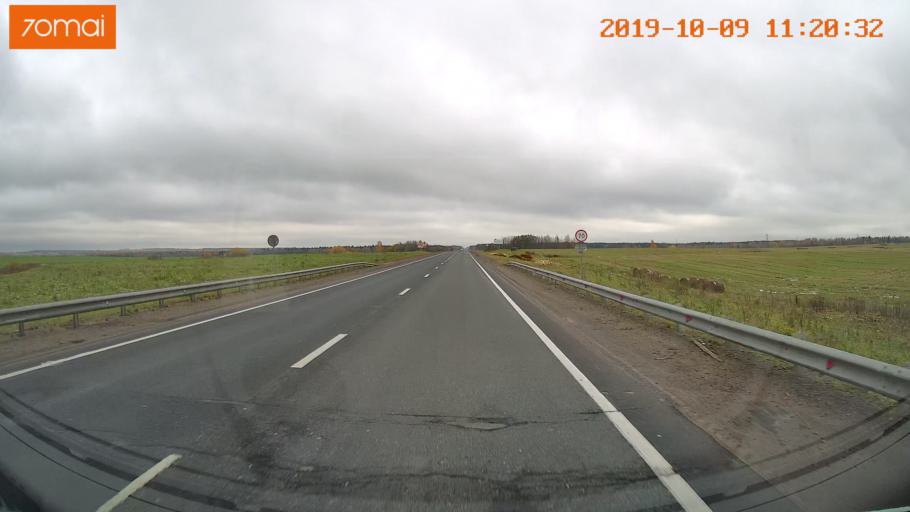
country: RU
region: Vologda
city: Vologda
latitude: 59.1486
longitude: 39.9396
